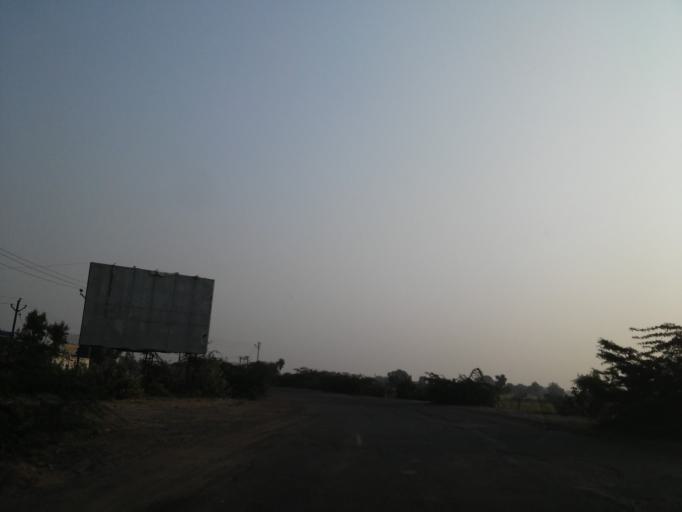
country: IN
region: Gujarat
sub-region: Kachchh
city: Bhachau
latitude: 23.3050
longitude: 70.3561
